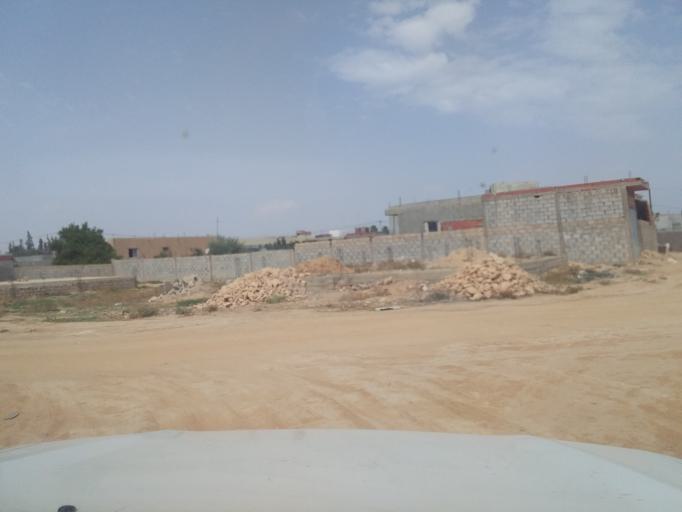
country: TN
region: Qabis
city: Matmata
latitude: 33.6137
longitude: 10.2778
